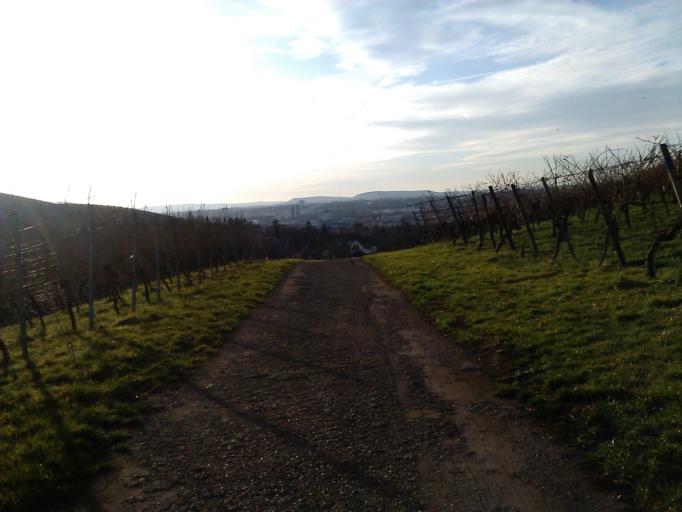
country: DE
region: Baden-Wuerttemberg
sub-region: Regierungsbezirk Stuttgart
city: Neckarsulm
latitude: 49.1659
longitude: 9.2378
